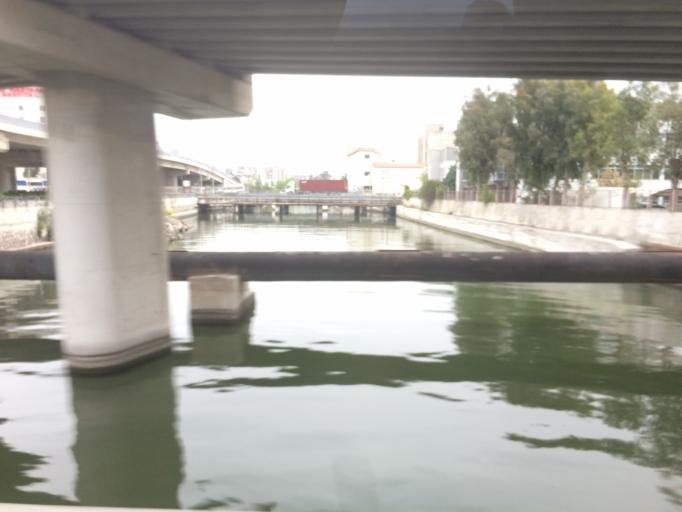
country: TR
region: Izmir
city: Izmir
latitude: 38.4594
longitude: 27.1656
